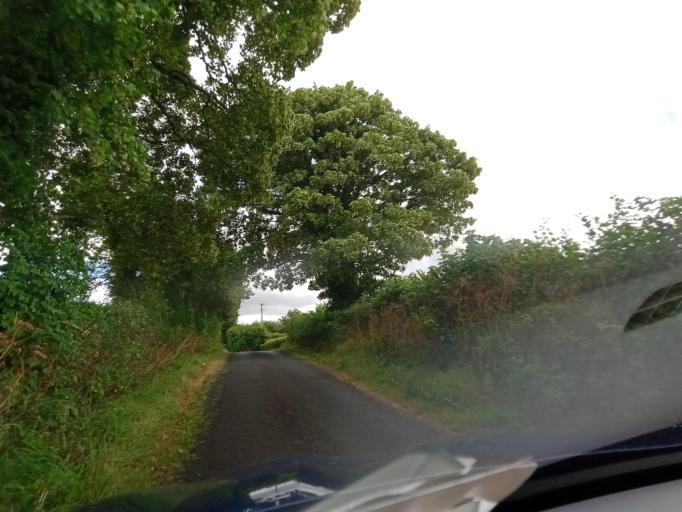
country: IE
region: Leinster
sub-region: Laois
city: Stradbally
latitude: 53.0288
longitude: -7.2130
